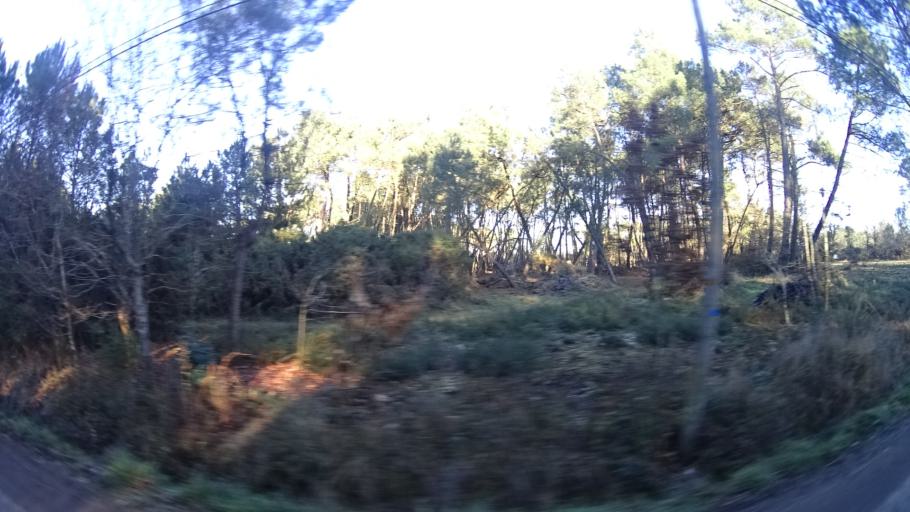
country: FR
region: Brittany
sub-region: Departement du Morbihan
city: Allaire
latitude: 47.6611
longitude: -2.1779
